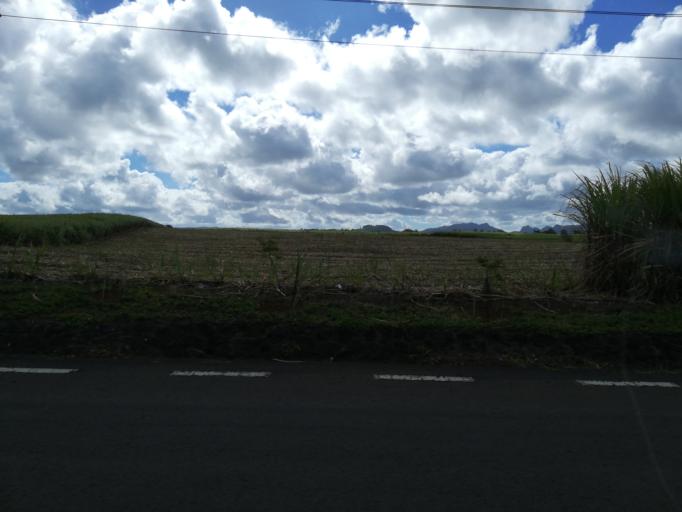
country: MU
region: Grand Port
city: Plaine Magnien
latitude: -20.4238
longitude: 57.6548
